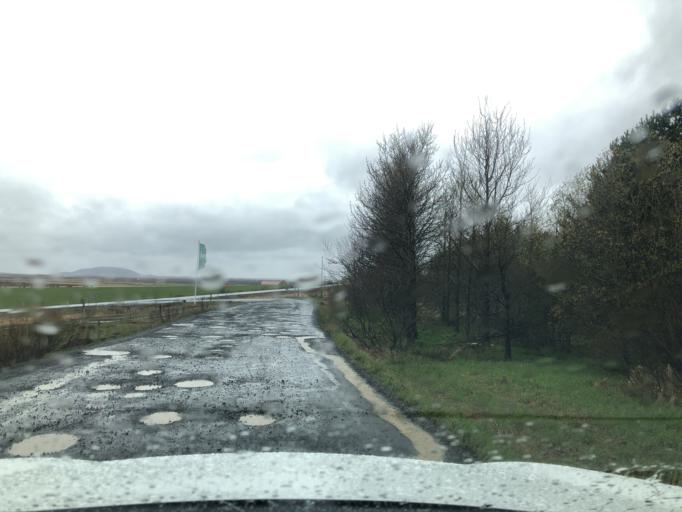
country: IS
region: South
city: Selfoss
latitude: 64.2399
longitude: -20.5498
